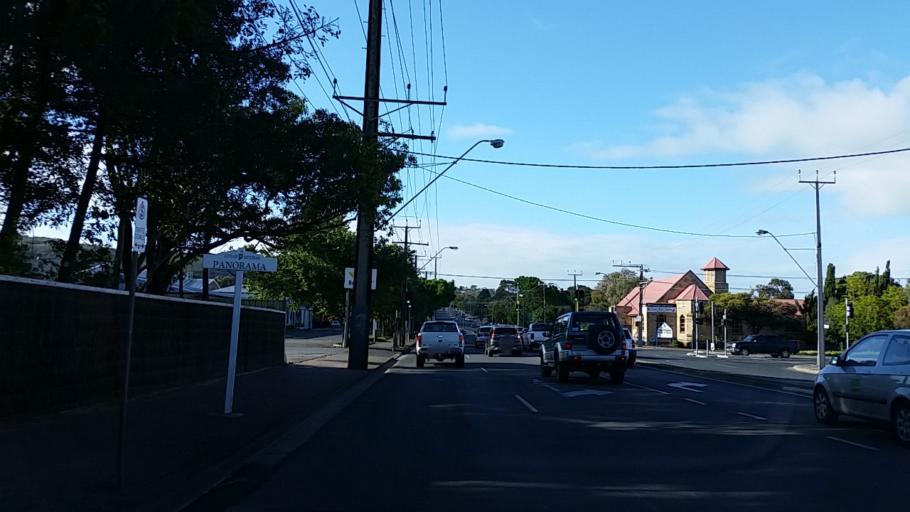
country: AU
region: South Australia
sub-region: Mitcham
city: Clapham
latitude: -34.9913
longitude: 138.5928
